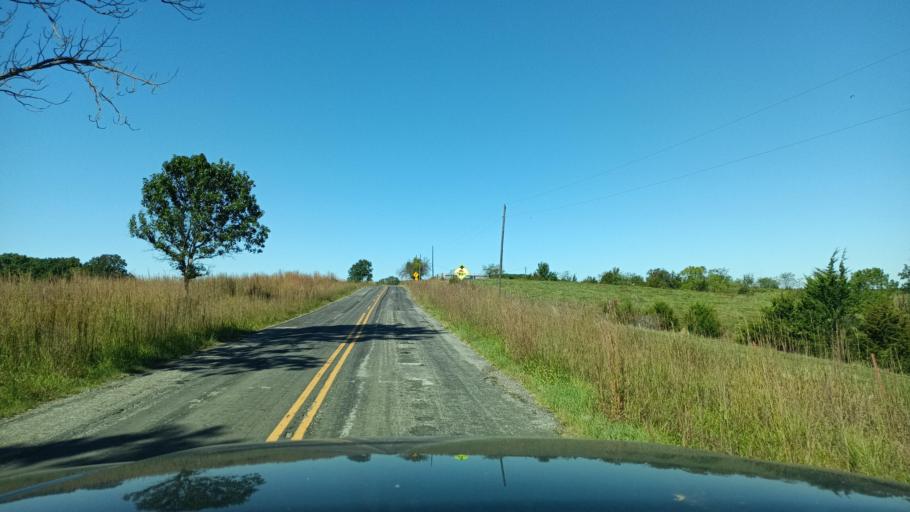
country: US
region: Missouri
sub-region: Scotland County
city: Memphis
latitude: 40.3491
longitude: -92.3345
